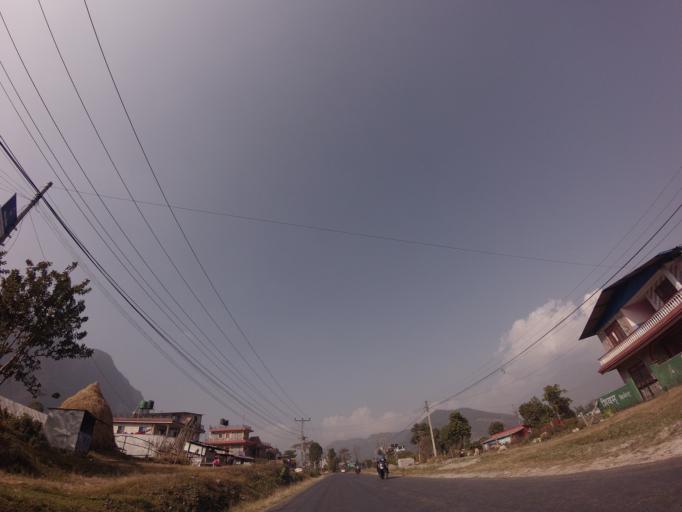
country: NP
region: Western Region
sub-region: Gandaki Zone
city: Pokhara
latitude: 28.2739
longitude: 83.9416
